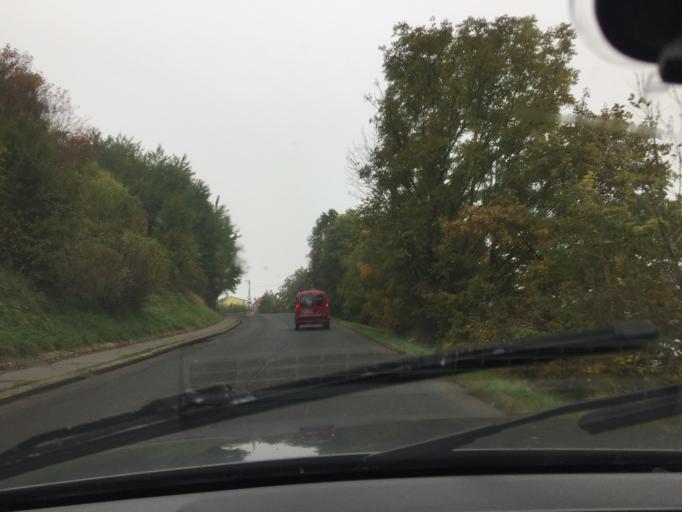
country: CZ
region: Ustecky
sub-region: Okres Usti nad Labem
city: Usti nad Labem
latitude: 50.6861
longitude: 14.0423
